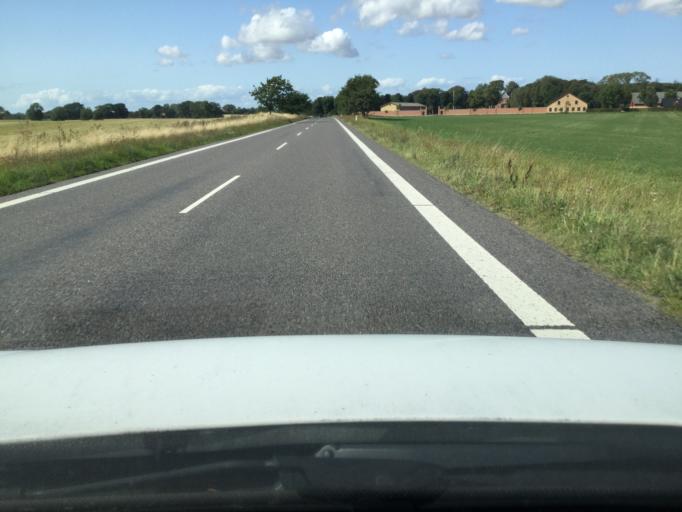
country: DK
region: Zealand
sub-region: Lolland Kommune
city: Rodby
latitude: 54.7834
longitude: 11.2924
